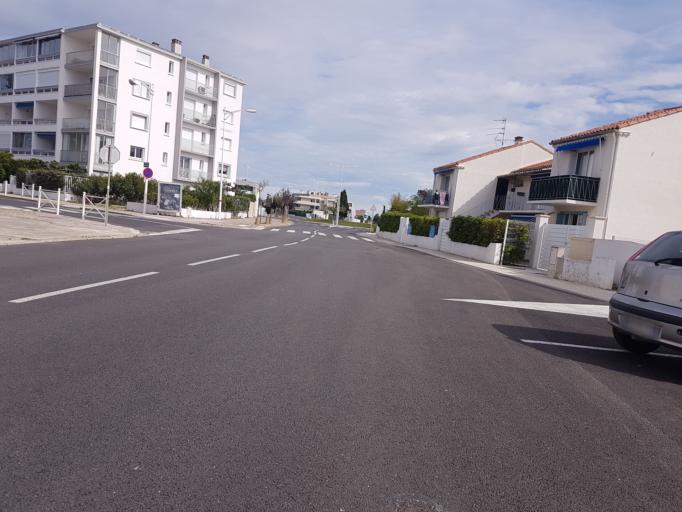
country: FR
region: Languedoc-Roussillon
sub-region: Departement du Gard
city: Le Grau-du-Roi
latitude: 43.5434
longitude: 4.1330
